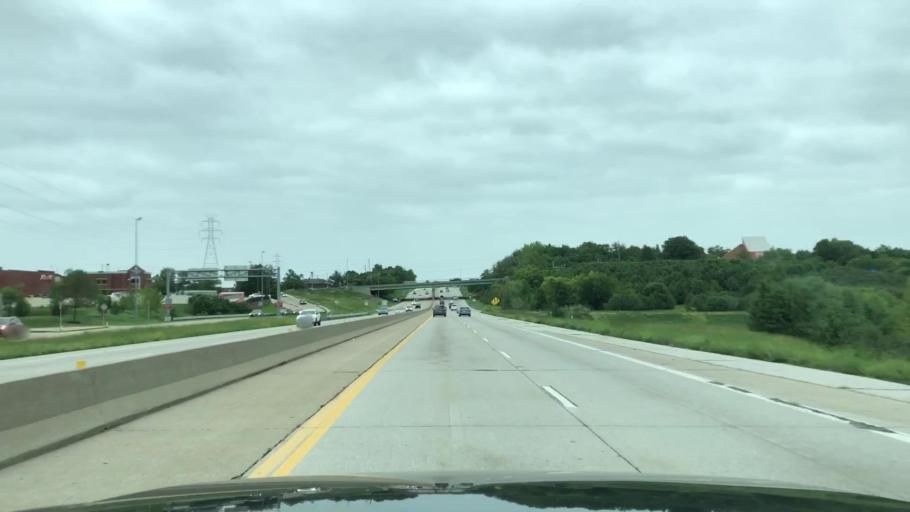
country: US
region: Missouri
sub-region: Saint Louis County
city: Manchester
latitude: 38.6218
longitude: -90.5111
